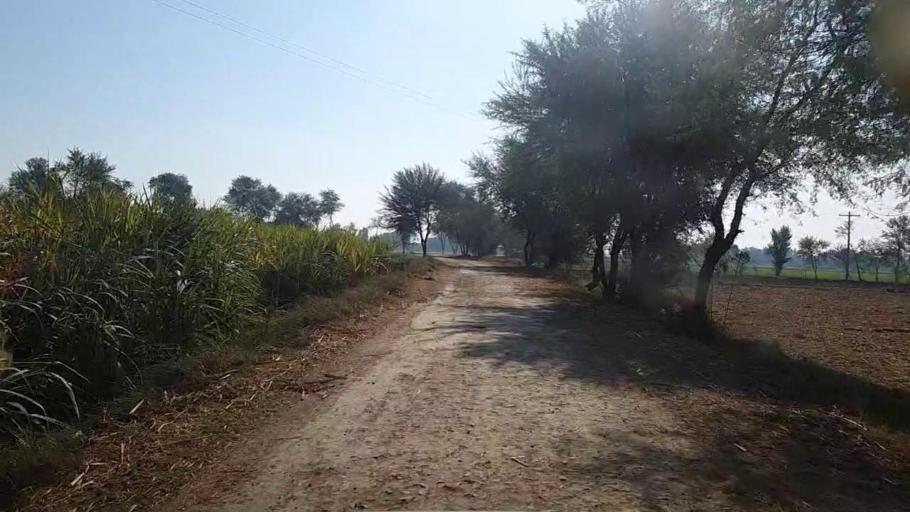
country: PK
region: Sindh
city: Khairpur
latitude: 28.0584
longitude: 69.7464
